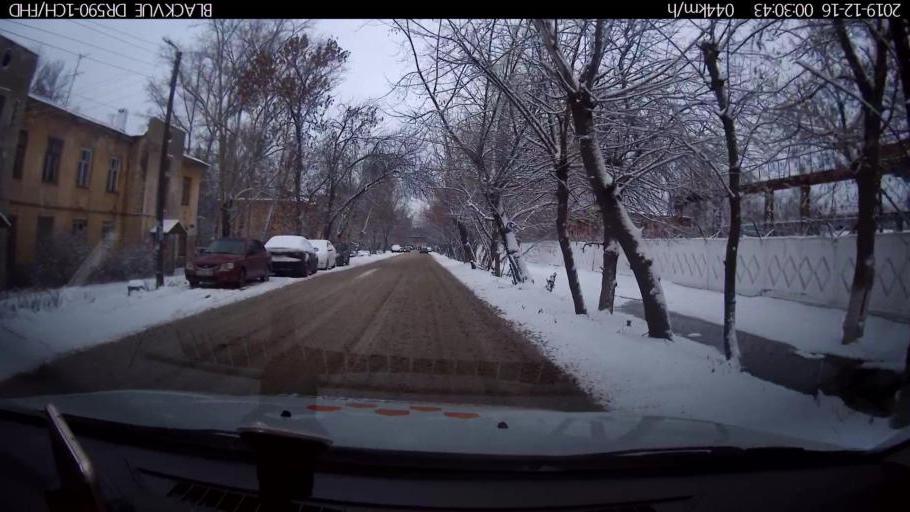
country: RU
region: Nizjnij Novgorod
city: Nizhniy Novgorod
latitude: 56.3113
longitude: 43.8904
